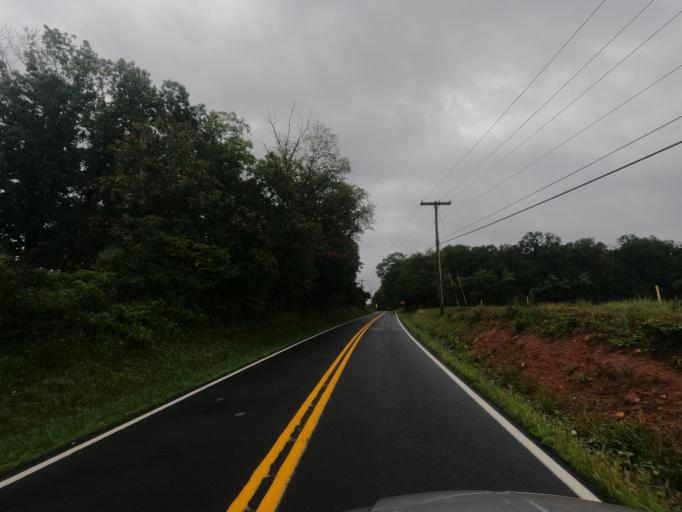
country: US
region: West Virginia
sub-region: Berkeley County
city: Martinsburg
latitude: 39.6184
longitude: -78.0044
